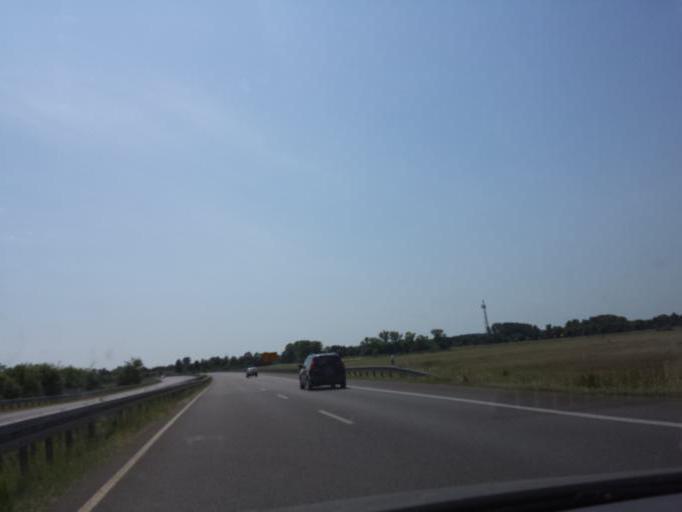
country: DE
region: Brandenburg
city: Leegebruch
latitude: 52.7547
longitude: 13.1999
